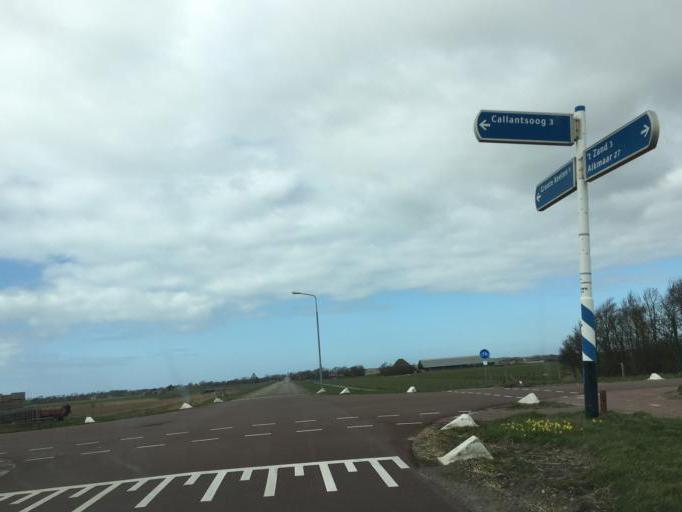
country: NL
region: North Holland
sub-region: Gemeente Schagen
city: Schagen
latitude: 52.8533
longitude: 4.7345
